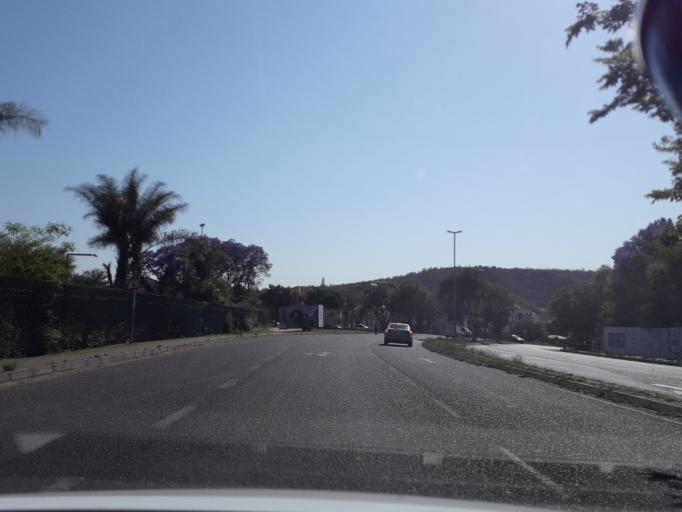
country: ZA
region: Gauteng
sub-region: City of Johannesburg Metropolitan Municipality
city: Roodepoort
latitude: -26.0961
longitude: 27.9442
